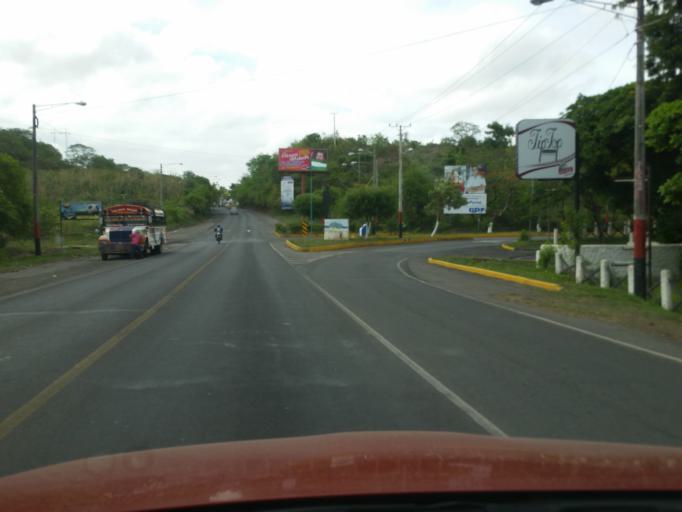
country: NI
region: Masaya
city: Nindiri
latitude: 11.9951
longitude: -86.1067
